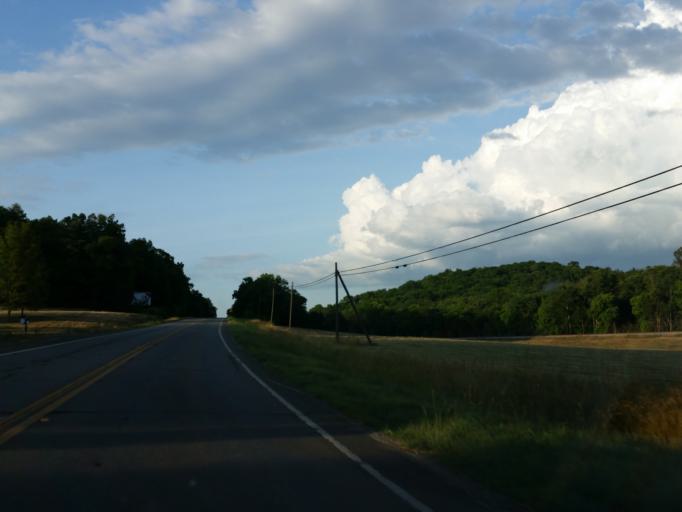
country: US
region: Georgia
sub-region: Dade County
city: Trenton
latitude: 34.9200
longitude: -85.4736
